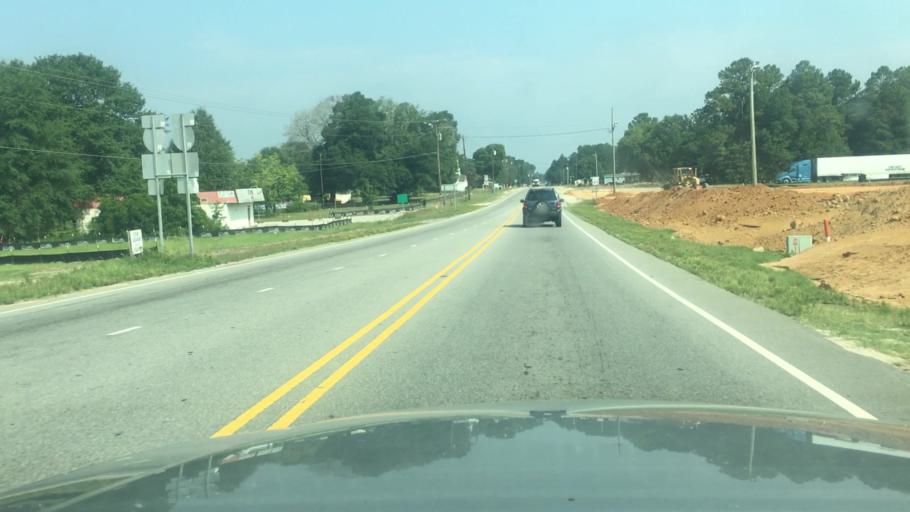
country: US
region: North Carolina
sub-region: Cumberland County
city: Hope Mills
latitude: 34.9462
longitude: -78.9322
